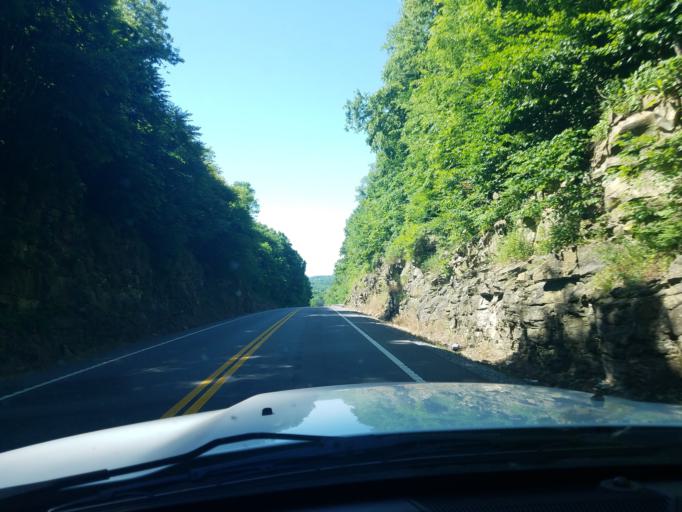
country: US
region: Tennessee
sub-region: Sumner County
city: Westmoreland
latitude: 36.4710
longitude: -86.2702
